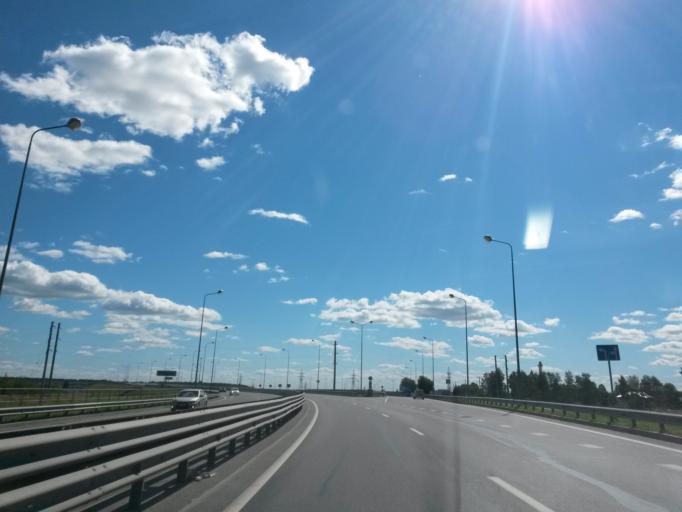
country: RU
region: Jaroslavl
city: Yaroslavl
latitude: 57.6916
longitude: 39.8984
